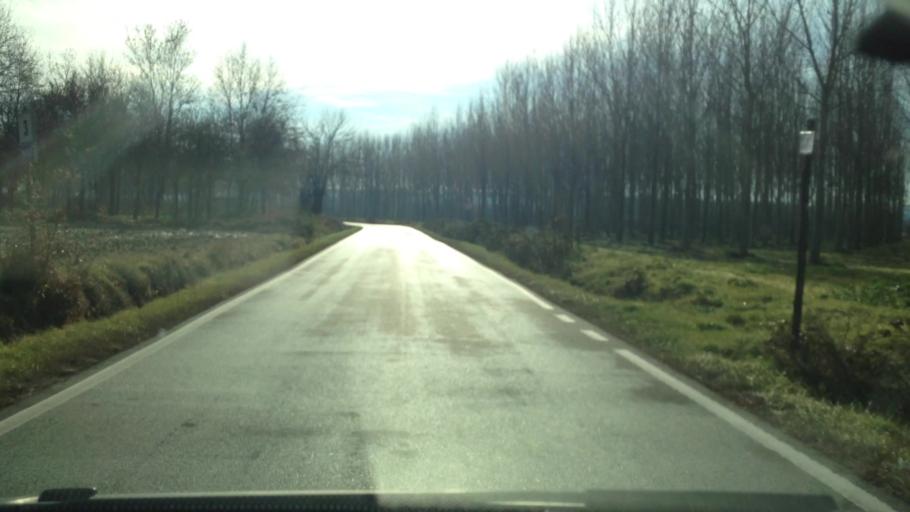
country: IT
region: Piedmont
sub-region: Provincia di Alessandria
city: Quattordio
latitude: 44.8875
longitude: 8.4044
